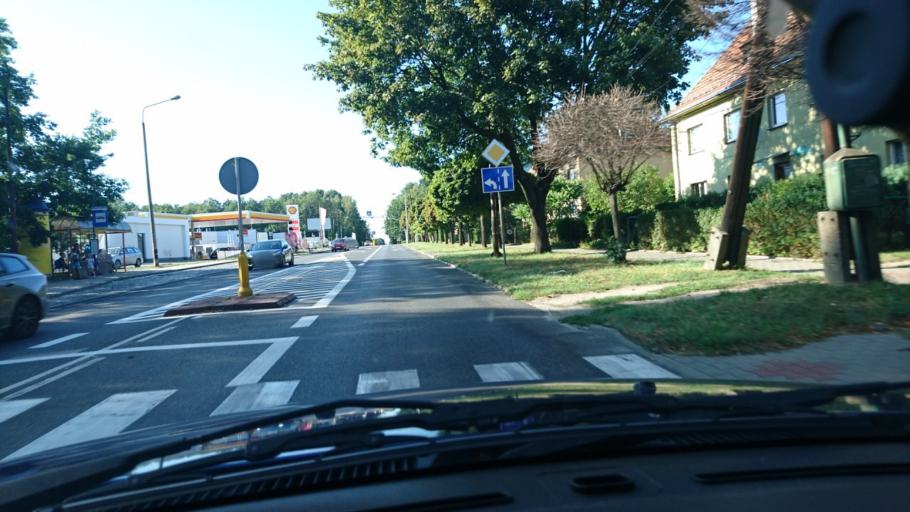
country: PL
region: Silesian Voivodeship
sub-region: Gliwice
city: Gliwice
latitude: 50.3237
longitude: 18.6621
